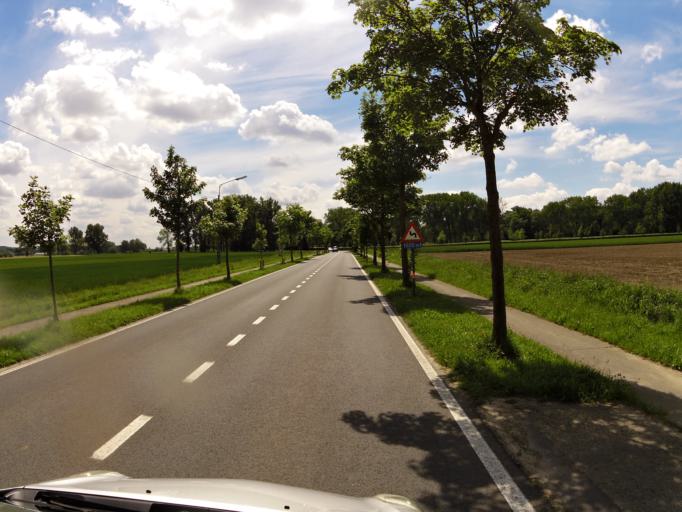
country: BE
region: Flanders
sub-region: Provincie West-Vlaanderen
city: Ieper
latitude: 50.8205
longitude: 2.8651
